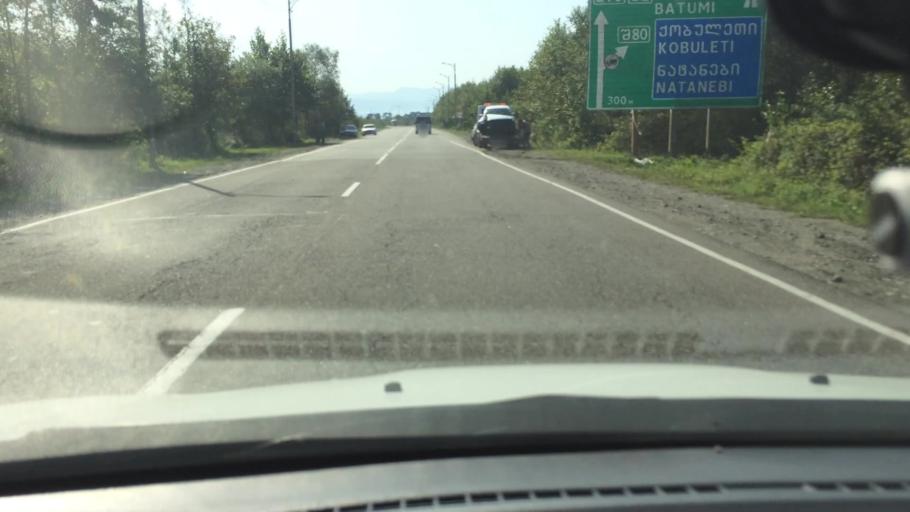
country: GE
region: Guria
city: Urek'i
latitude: 41.9280
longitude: 41.7730
